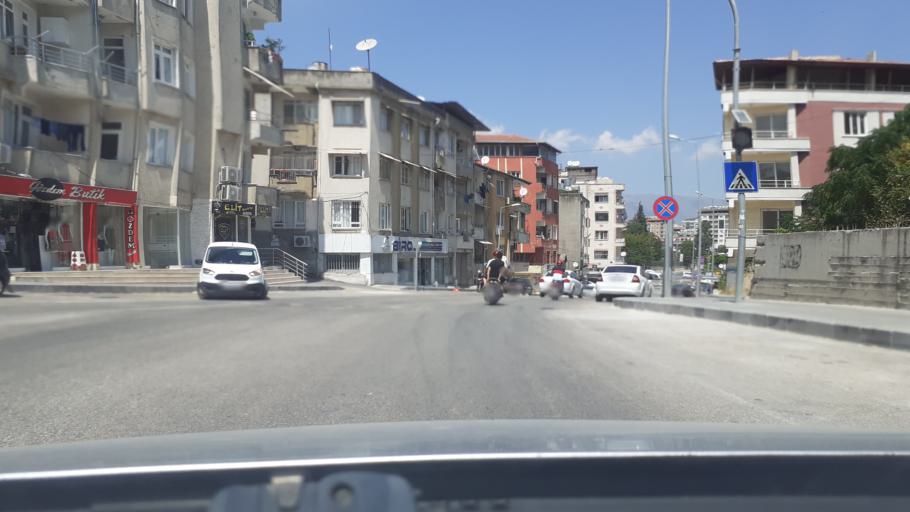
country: TR
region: Hatay
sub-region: Antakya Ilcesi
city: Antakya
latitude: 36.1980
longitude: 36.1545
